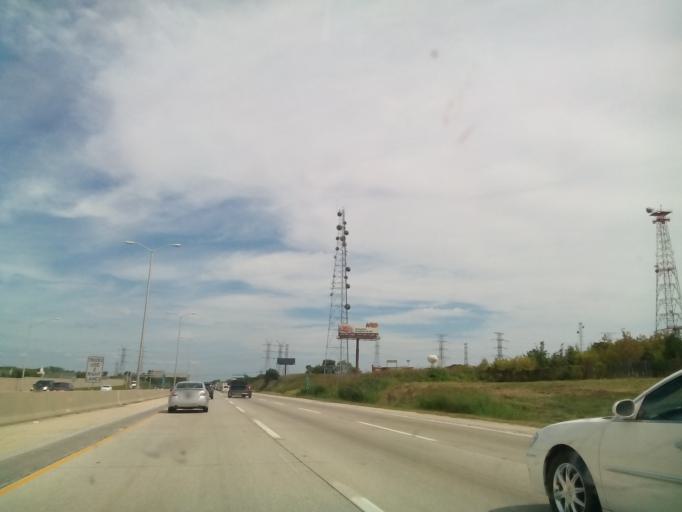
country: US
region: Illinois
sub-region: DuPage County
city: Warrenville
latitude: 41.8009
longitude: -88.2397
